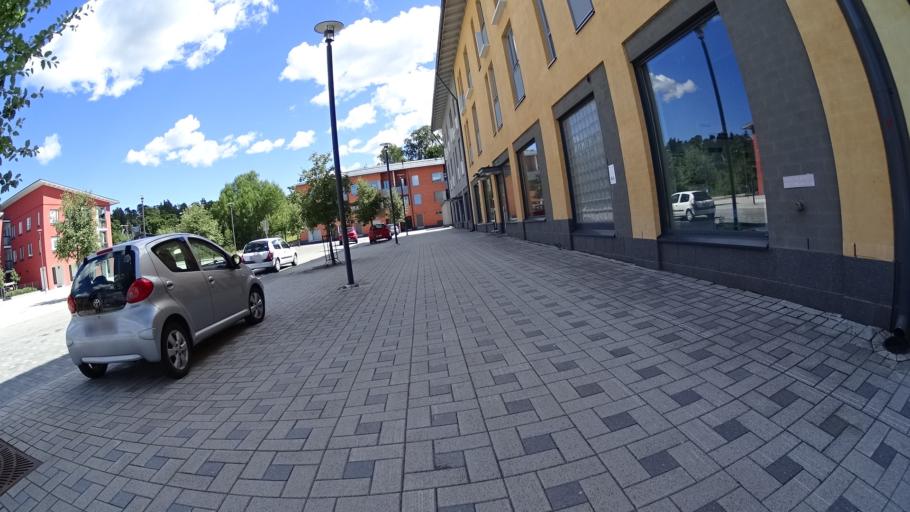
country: FI
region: Uusimaa
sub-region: Helsinki
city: Espoo
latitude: 60.1925
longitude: 24.5987
